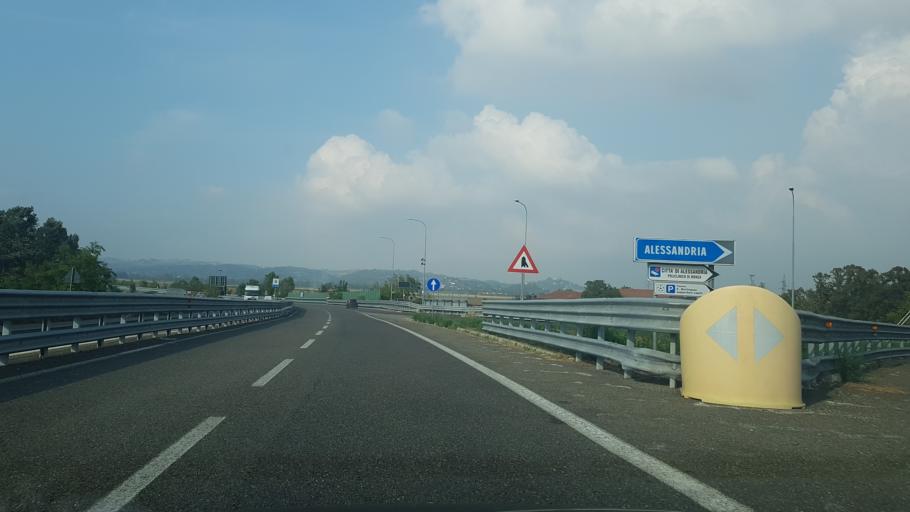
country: IT
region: Piedmont
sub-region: Provincia di Alessandria
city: Alessandria
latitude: 44.9102
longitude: 8.6422
